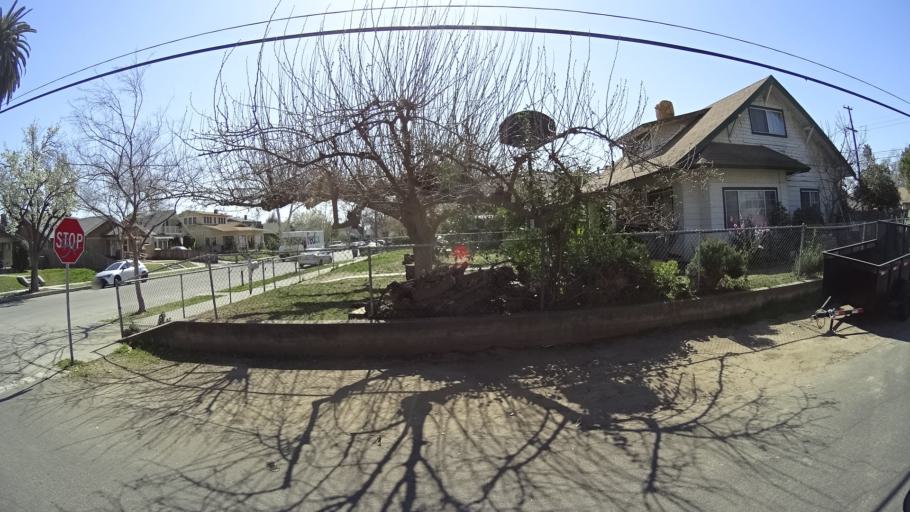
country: US
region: California
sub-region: Fresno County
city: Fresno
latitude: 36.7540
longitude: -119.8053
